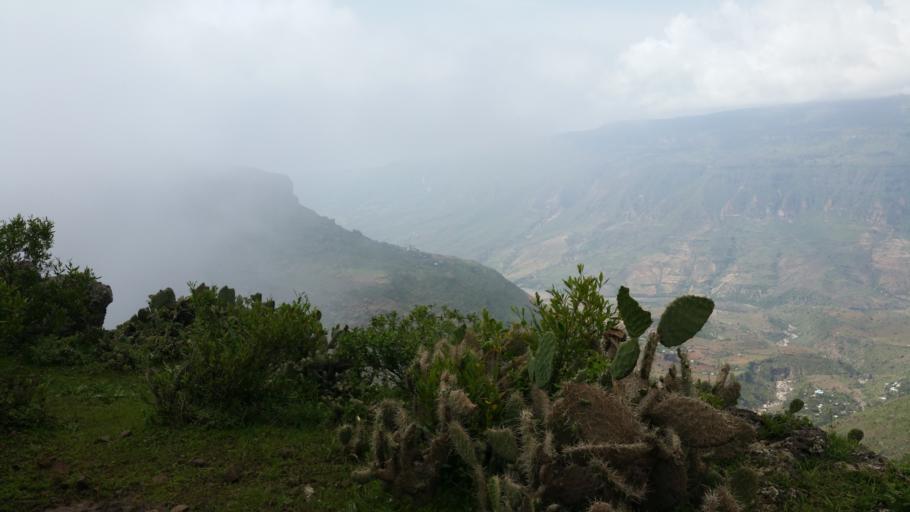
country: ET
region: Oromiya
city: Fiche
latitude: 9.7340
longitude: 38.8156
